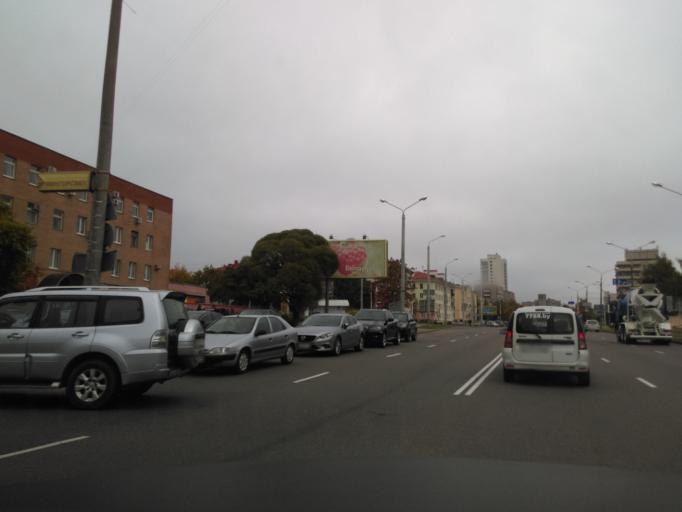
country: BY
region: Minsk
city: Minsk
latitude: 53.9048
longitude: 27.5899
